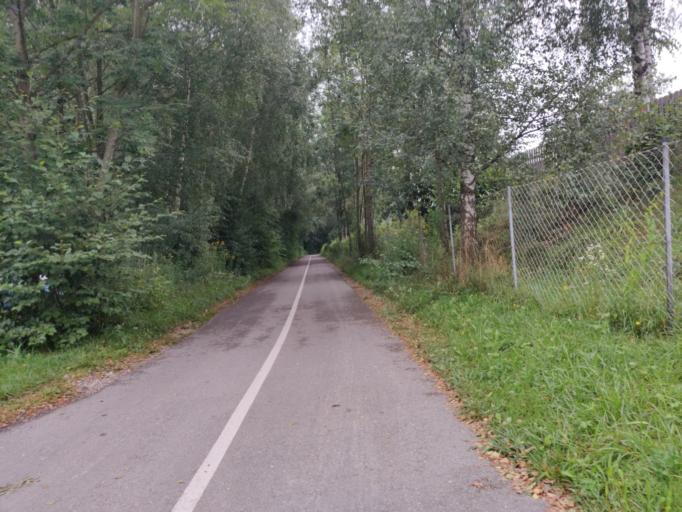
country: AT
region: Upper Austria
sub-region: Politischer Bezirk Urfahr-Umgebung
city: Steyregg
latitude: 48.2709
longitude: 14.3831
